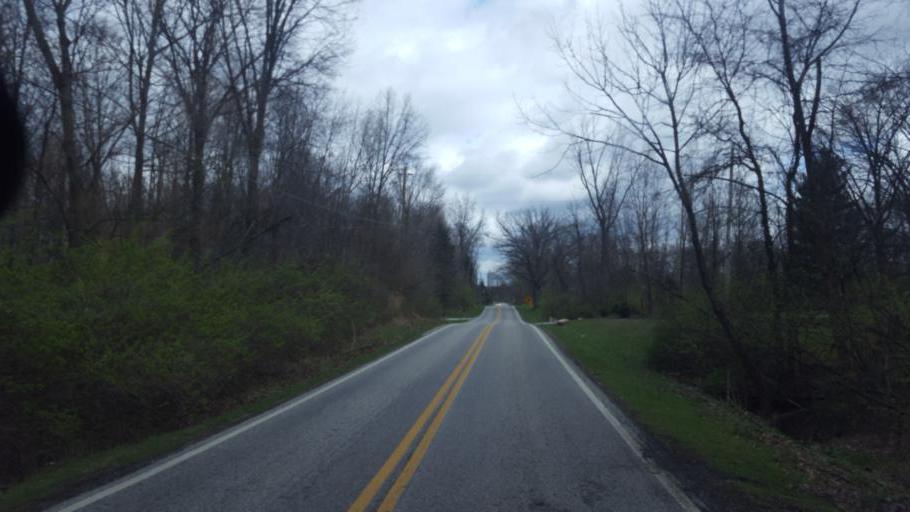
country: US
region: Ohio
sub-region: Franklin County
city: Westerville
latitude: 40.1658
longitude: -82.8635
